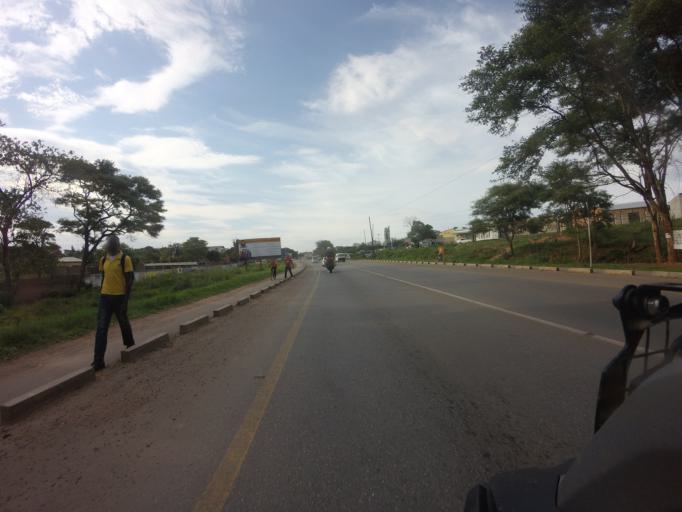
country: ZM
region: Lusaka
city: Lusaka
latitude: -15.5562
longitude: 28.2728
